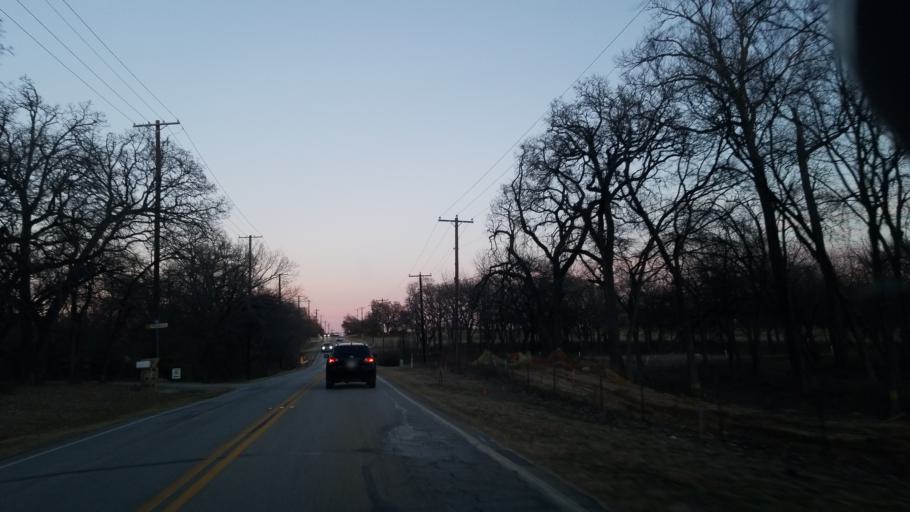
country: US
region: Texas
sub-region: Denton County
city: Denton
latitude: 33.1615
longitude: -97.1251
